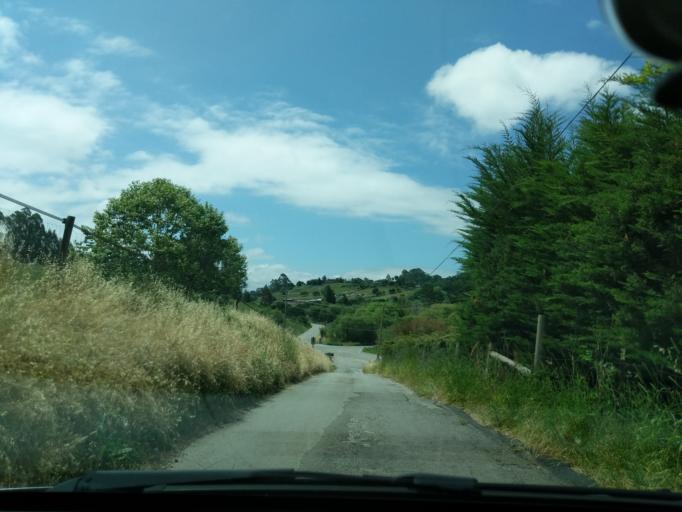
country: US
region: California
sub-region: Santa Cruz County
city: Aptos Hills-Larkin Valley
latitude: 36.9389
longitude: -121.8082
